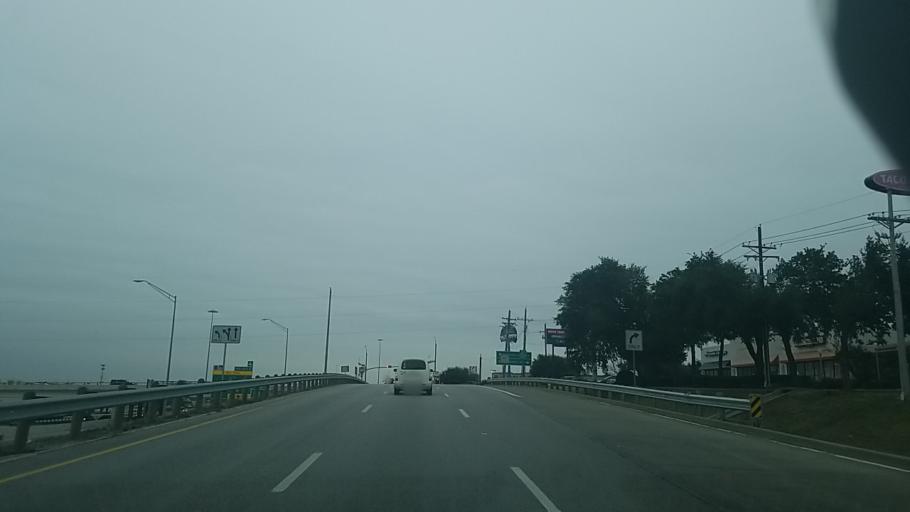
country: US
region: Texas
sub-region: Denton County
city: Lewisville
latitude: 33.0073
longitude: -96.9739
